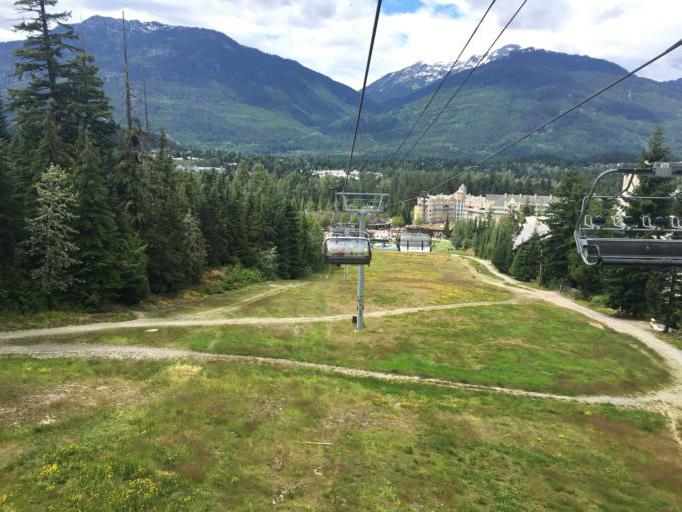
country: CA
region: British Columbia
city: Whistler
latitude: 50.1140
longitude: -122.9436
